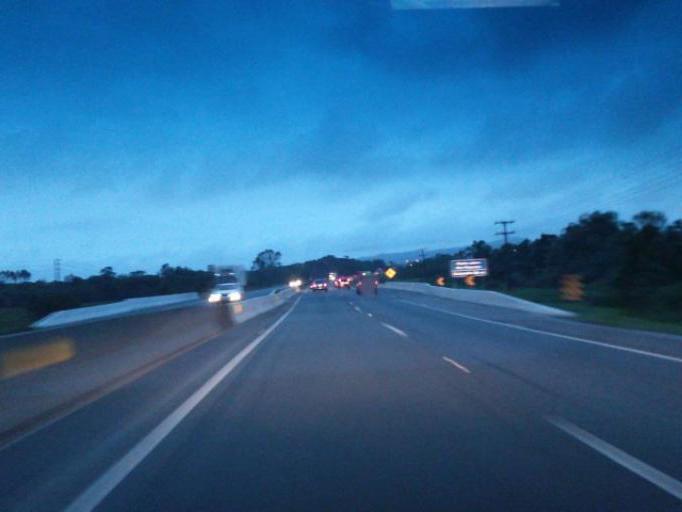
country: BR
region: Santa Catarina
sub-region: Penha
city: Penha
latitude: -26.7500
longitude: -48.6937
